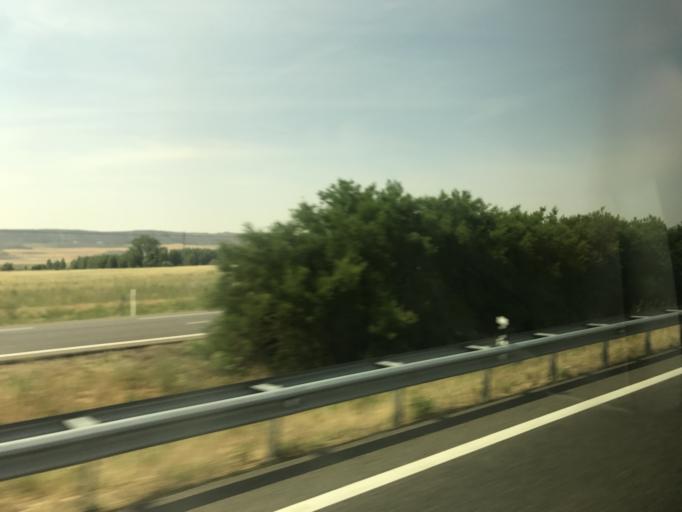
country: ES
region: Castille and Leon
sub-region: Provincia de Palencia
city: Palenzuela
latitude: 42.1282
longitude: -4.1327
